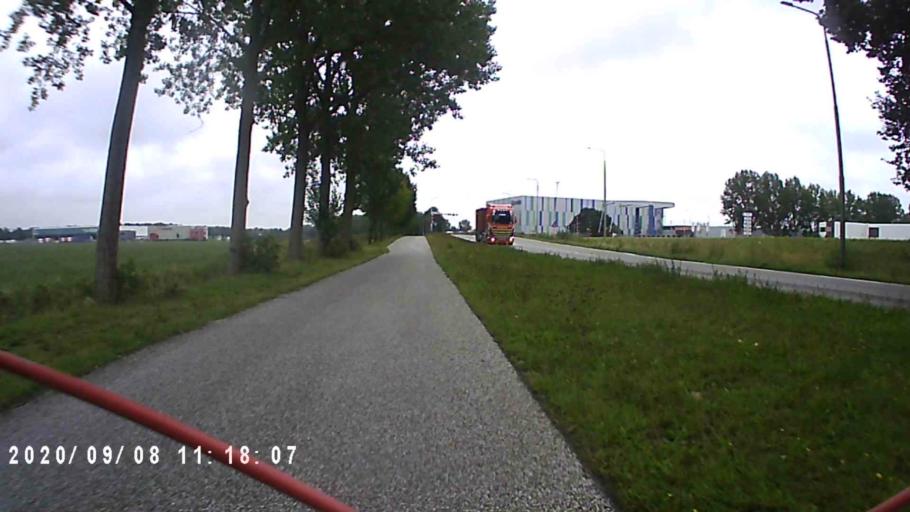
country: NL
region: Groningen
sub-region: Gemeente Hoogezand-Sappemeer
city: Hoogezand
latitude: 53.1695
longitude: 6.7412
